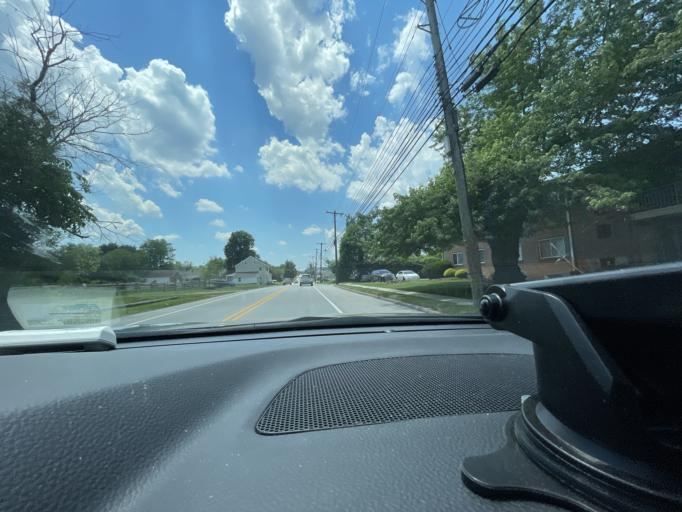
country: US
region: Pennsylvania
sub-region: Montgomery County
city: Plymouth Meeting
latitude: 40.0987
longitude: -75.2824
